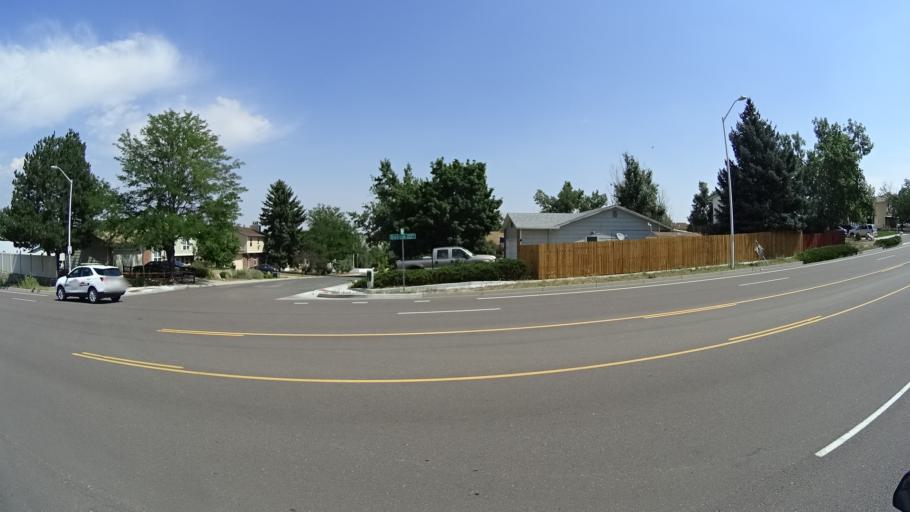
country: US
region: Colorado
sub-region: El Paso County
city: Cimarron Hills
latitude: 38.9253
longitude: -104.7704
